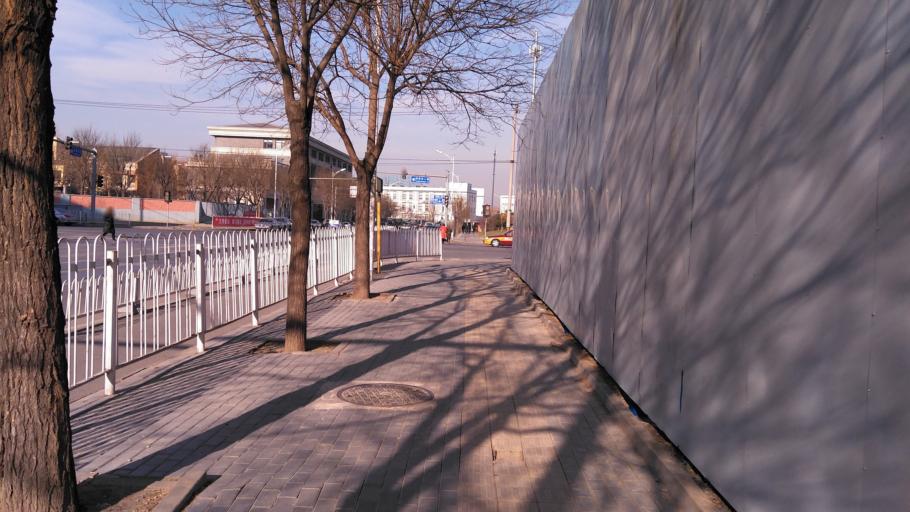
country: CN
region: Beijing
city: Wangjing
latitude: 40.0069
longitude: 116.4765
